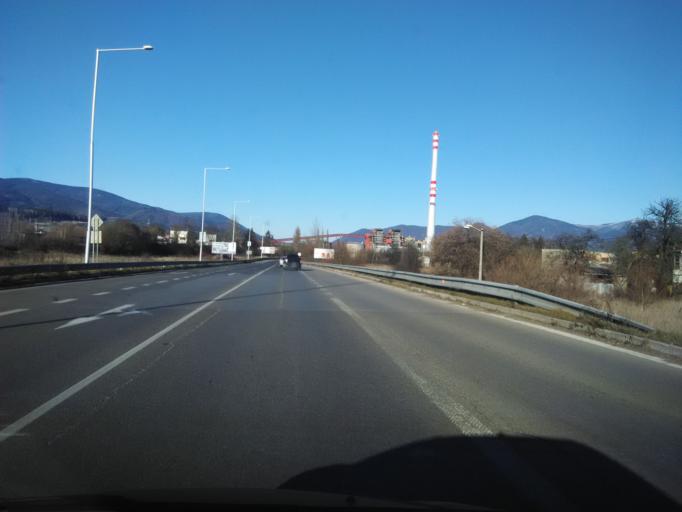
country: SK
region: Zilinsky
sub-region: Okres Martin
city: Martin
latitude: 49.0522
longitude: 18.9064
